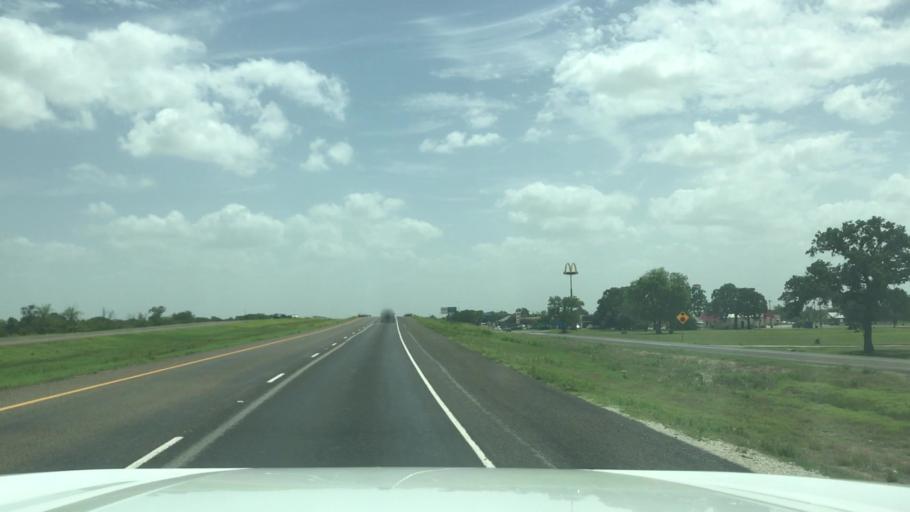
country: US
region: Texas
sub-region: Falls County
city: Marlin
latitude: 31.3094
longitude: -96.8748
